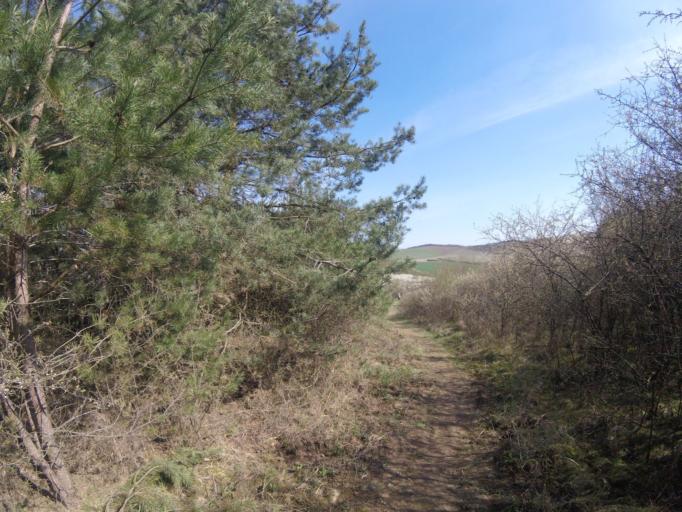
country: HU
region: Borsod-Abauj-Zemplen
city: Szendro
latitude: 48.4102
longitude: 20.7362
